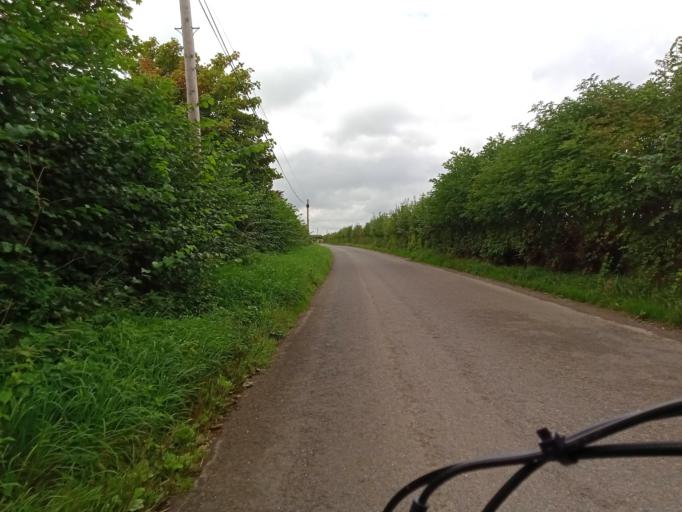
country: IE
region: Leinster
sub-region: Kilkenny
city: Callan
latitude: 52.5358
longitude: -7.2786
